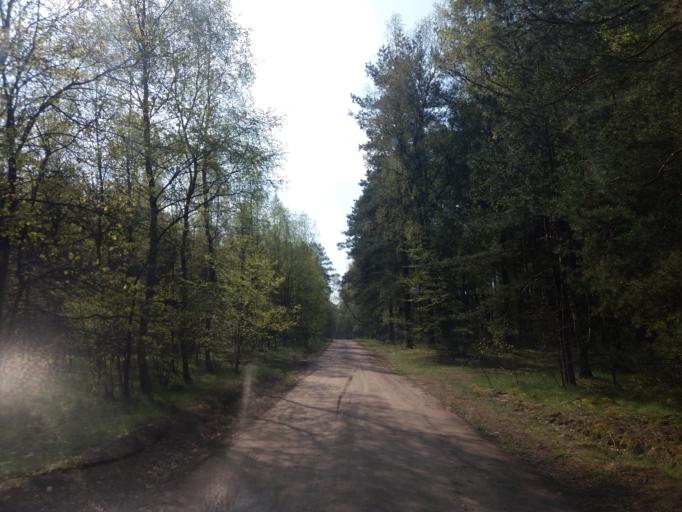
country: PL
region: West Pomeranian Voivodeship
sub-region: Powiat choszczenski
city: Drawno
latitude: 53.2170
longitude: 15.8279
